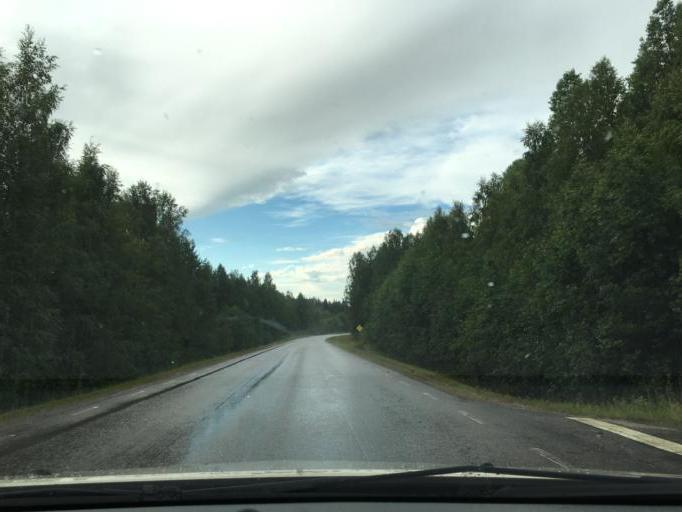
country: SE
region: Norrbotten
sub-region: Kalix Kommun
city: Toere
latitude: 65.9930
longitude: 22.8585
